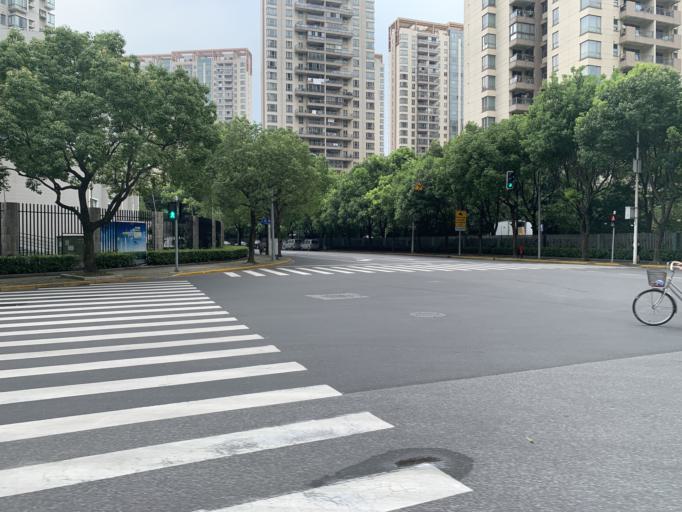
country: CN
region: Shanghai Shi
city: Huamu
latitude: 31.2300
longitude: 121.5611
